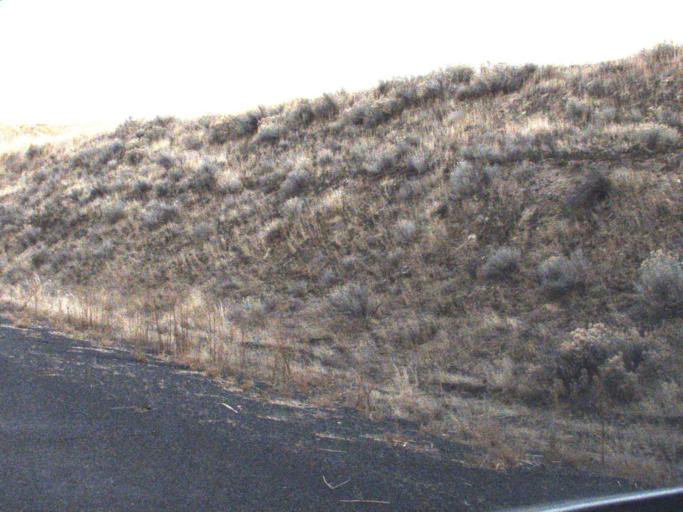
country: US
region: Washington
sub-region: Adams County
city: Ritzville
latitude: 46.7807
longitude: -118.3813
